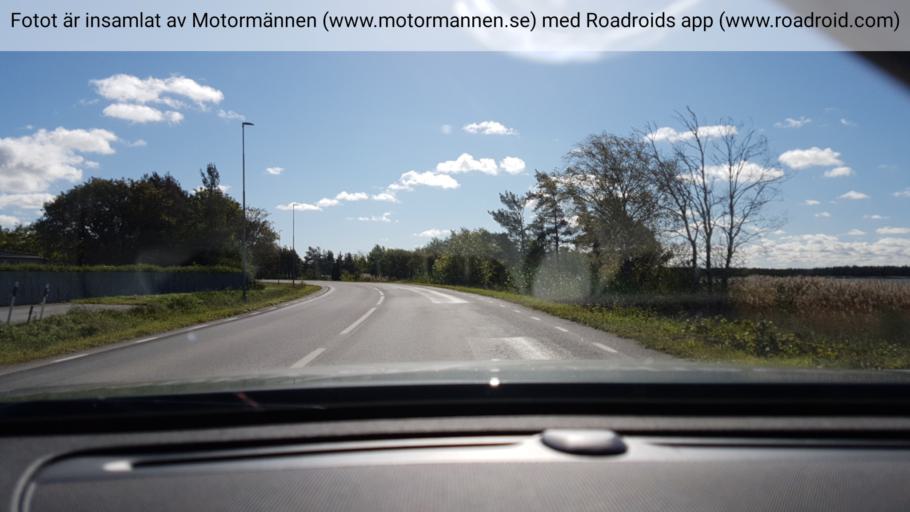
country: SE
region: Gotland
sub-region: Gotland
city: Slite
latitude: 57.6995
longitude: 18.7949
